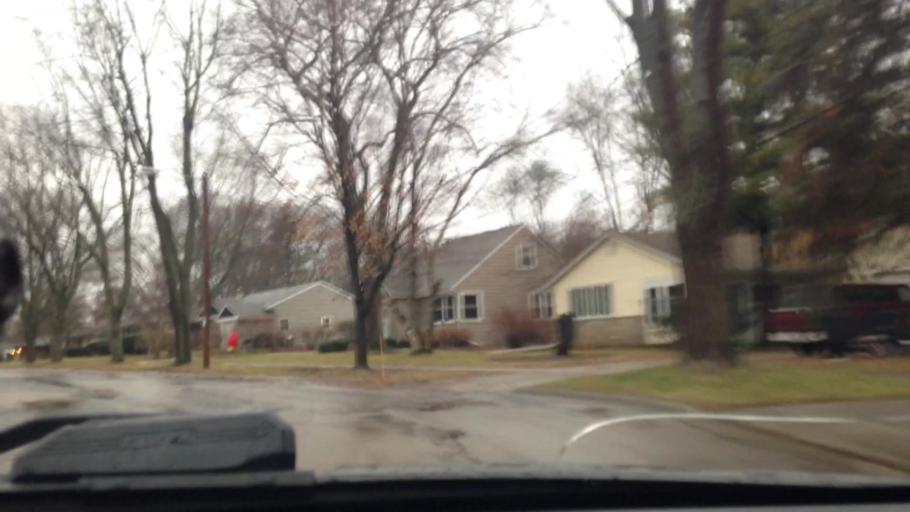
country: US
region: Wisconsin
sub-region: Waukesha County
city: Menomonee Falls
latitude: 43.1747
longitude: -88.1174
